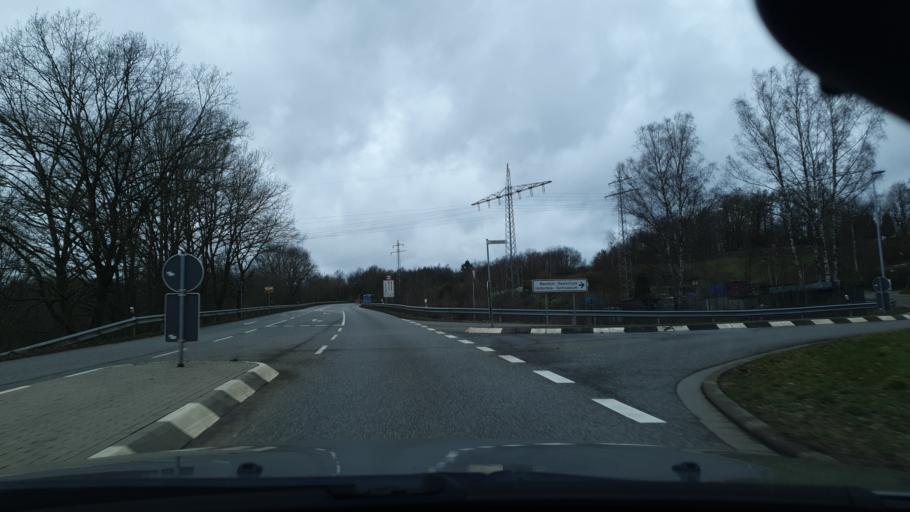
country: DE
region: Rheinland-Pfalz
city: Zweibrucken
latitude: 49.2596
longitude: 7.3791
